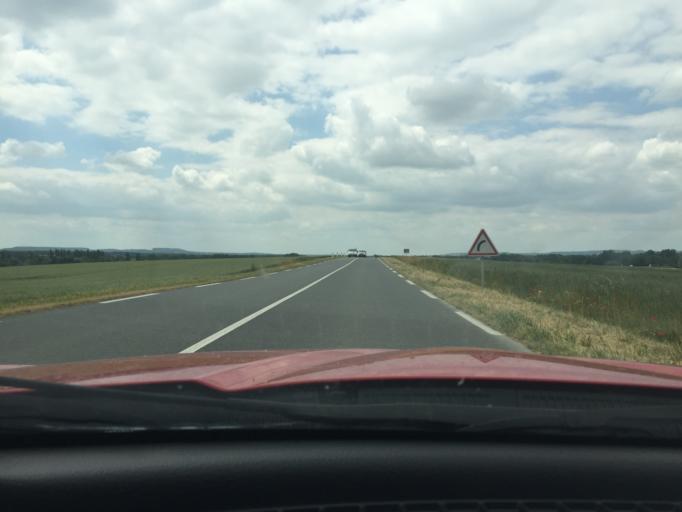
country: FR
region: Champagne-Ardenne
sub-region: Departement de la Marne
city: Cormicy
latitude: 49.4140
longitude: 3.8987
